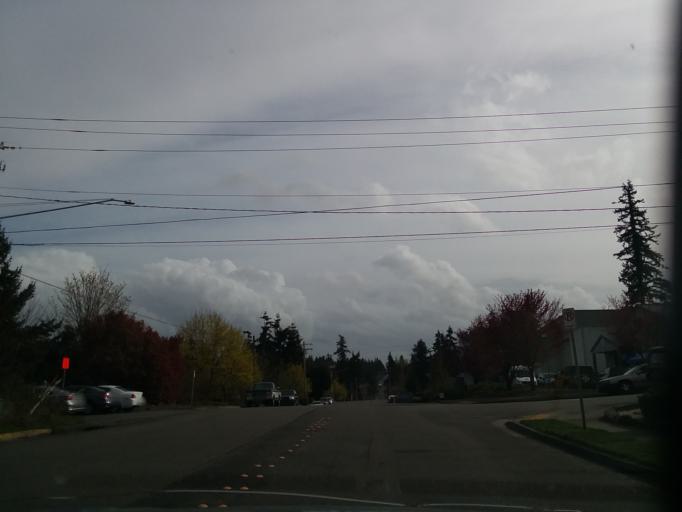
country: US
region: Washington
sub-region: Snohomish County
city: Lynnwood
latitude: 47.8088
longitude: -122.3220
